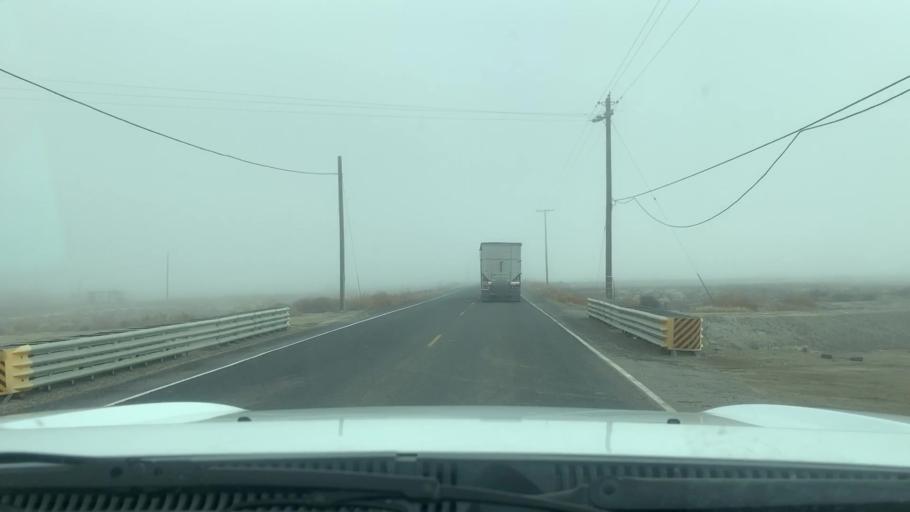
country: US
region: California
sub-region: Kern County
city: Buttonwillow
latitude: 35.4997
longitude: -119.5667
